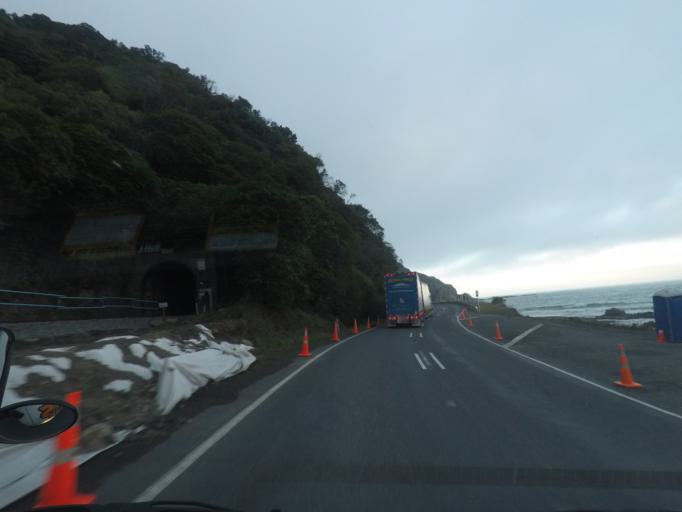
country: NZ
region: Canterbury
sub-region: Kaikoura District
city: Kaikoura
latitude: -42.4520
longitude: 173.5676
